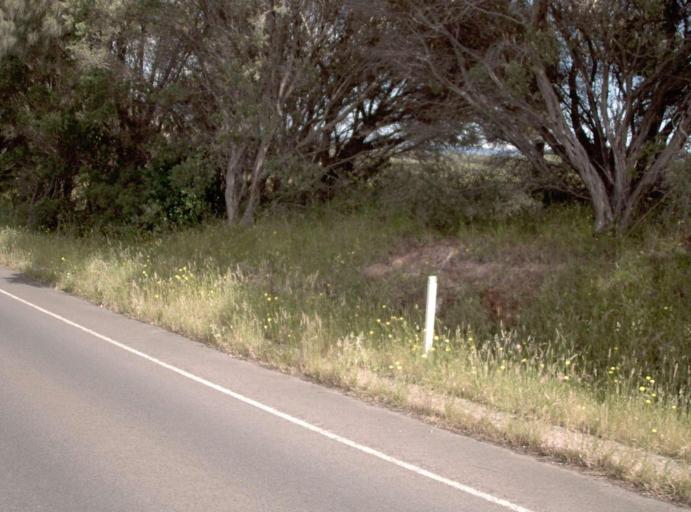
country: AU
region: Victoria
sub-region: Bass Coast
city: Phillip Island
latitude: -38.4967
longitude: 145.2236
